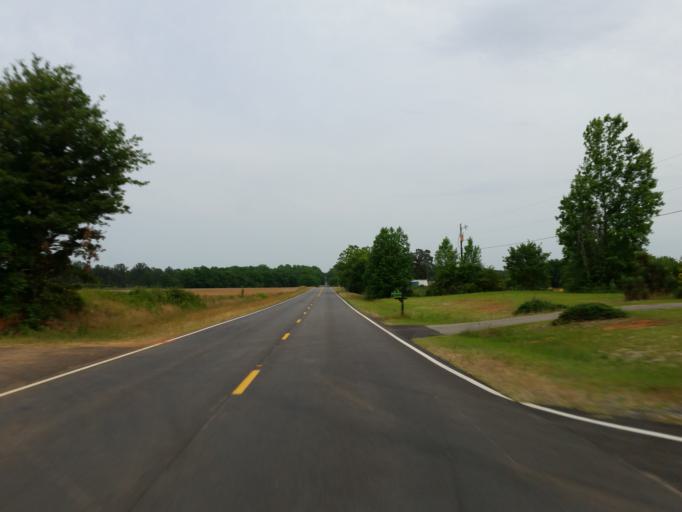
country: US
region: Georgia
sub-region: Dooly County
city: Unadilla
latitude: 32.3071
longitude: -83.7660
